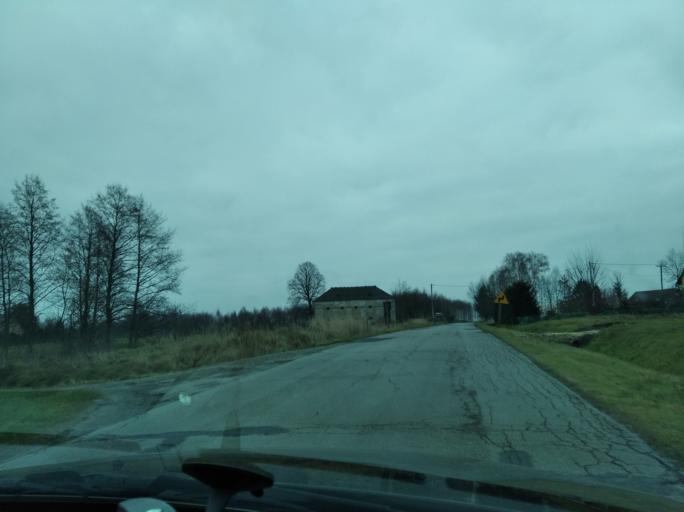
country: PL
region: Subcarpathian Voivodeship
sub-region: Powiat lancucki
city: Brzoza Stadnicka
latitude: 50.2041
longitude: 22.2995
